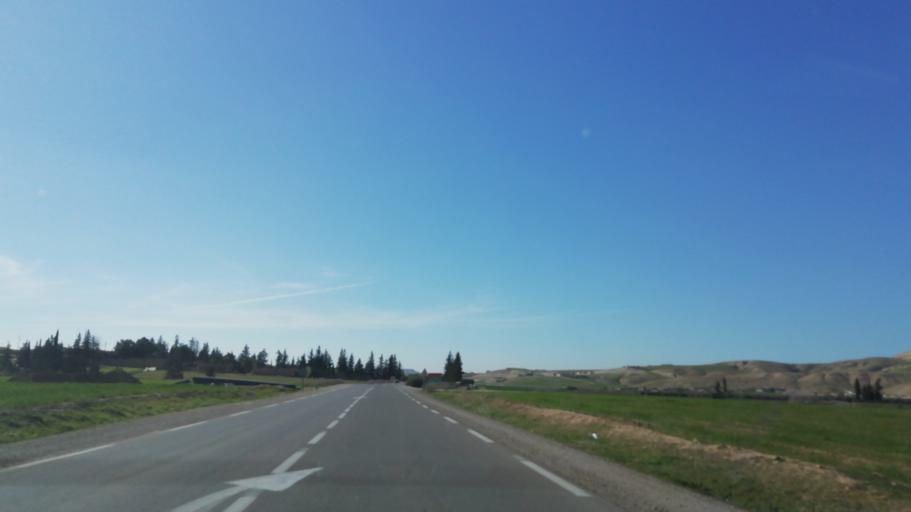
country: DZ
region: Mascara
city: Oued el Abtal
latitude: 35.4571
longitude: 0.7570
